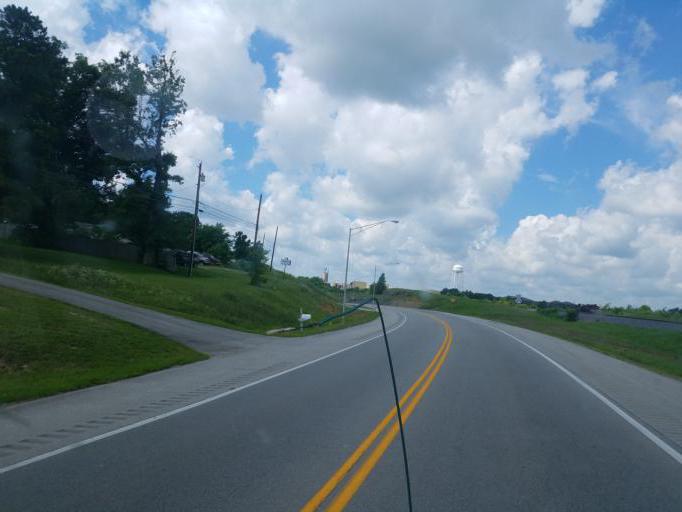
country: US
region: Kentucky
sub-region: Grayson County
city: Leitchfield
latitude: 37.4894
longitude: -86.2607
